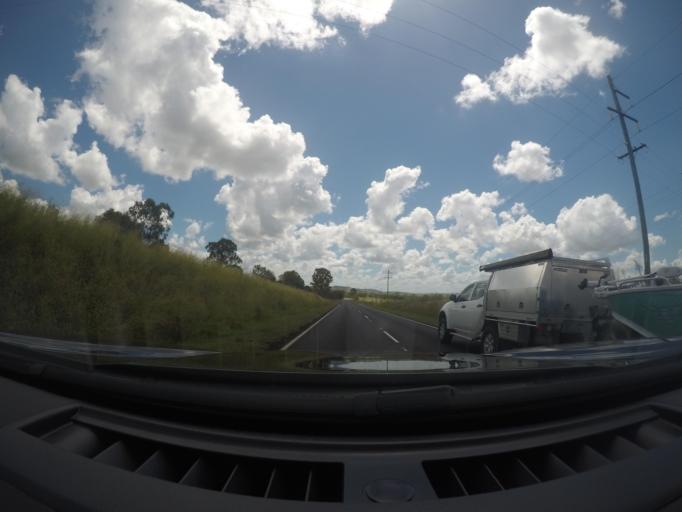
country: AU
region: Queensland
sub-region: Moreton Bay
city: Woodford
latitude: -27.1426
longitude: 152.4921
